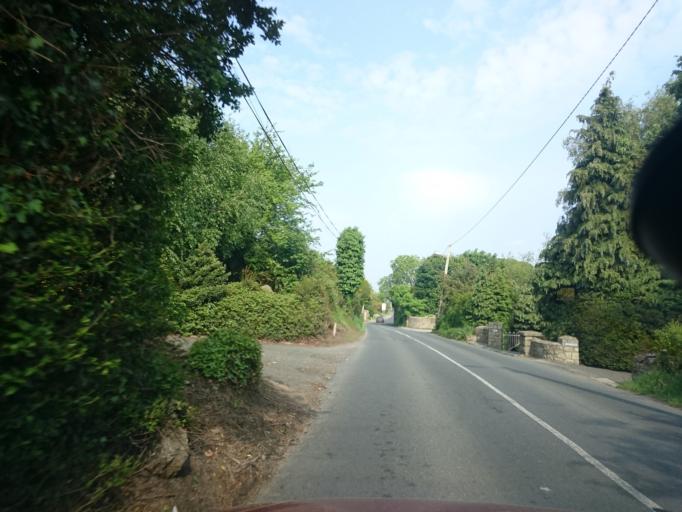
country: IE
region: Leinster
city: Balally
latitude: 53.2665
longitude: -6.2445
